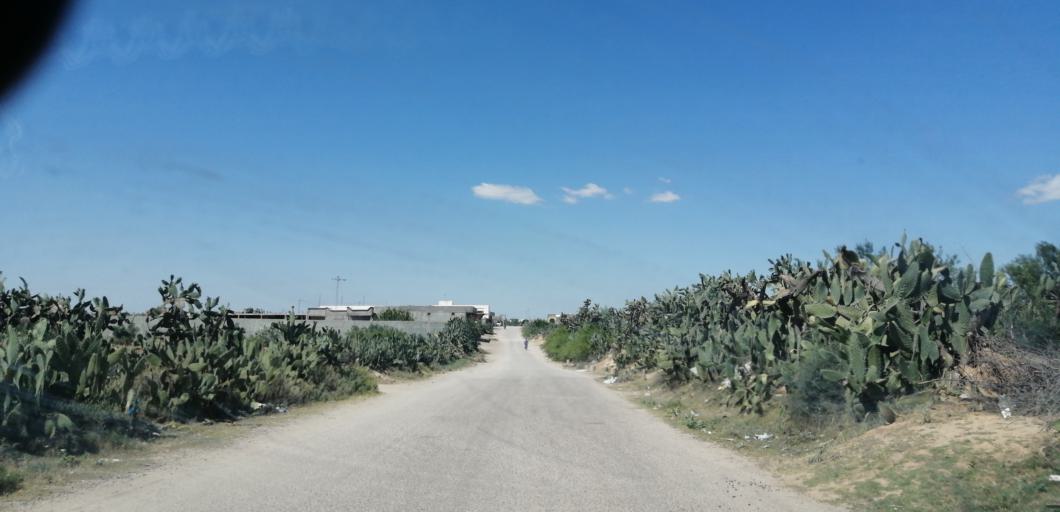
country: TN
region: Al Qayrawan
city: Kairouan
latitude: 35.6266
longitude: 9.9307
